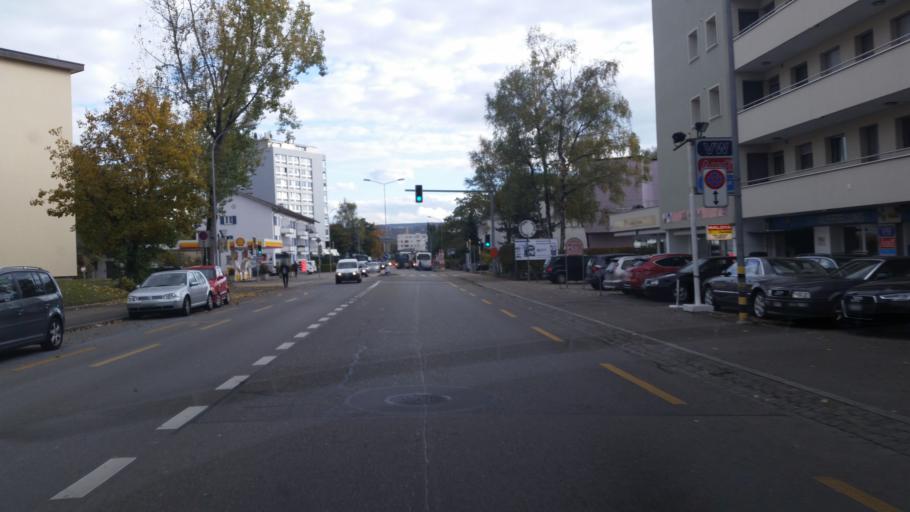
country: CH
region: Zurich
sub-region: Bezirk Zuerich
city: Zuerich (Kreis 11) / Seebach
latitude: 47.4264
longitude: 8.5470
